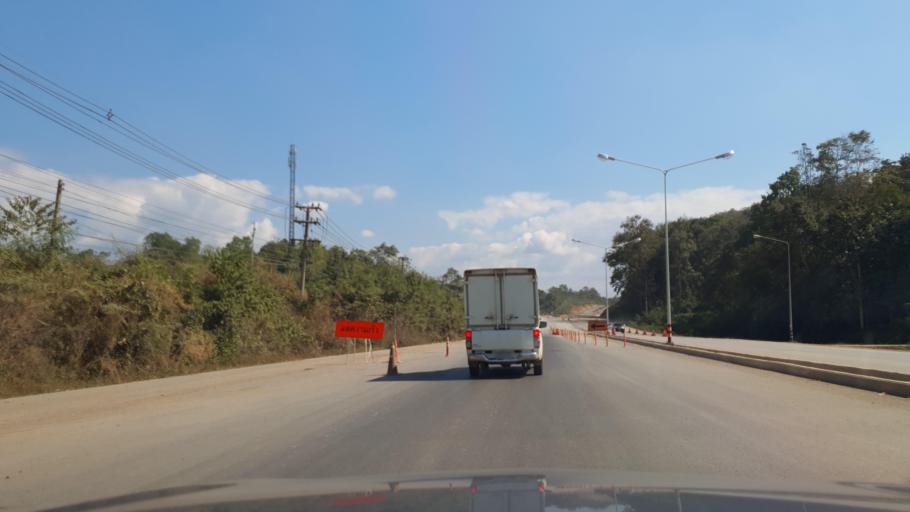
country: TH
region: Nan
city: Nan
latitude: 18.8292
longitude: 100.7569
